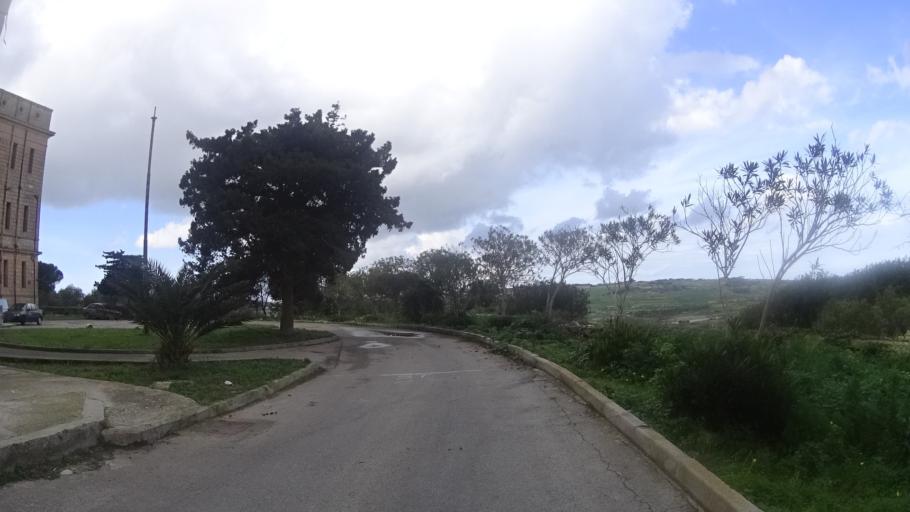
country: MT
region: L-Imtarfa
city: Imtarfa
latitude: 35.8907
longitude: 14.3958
